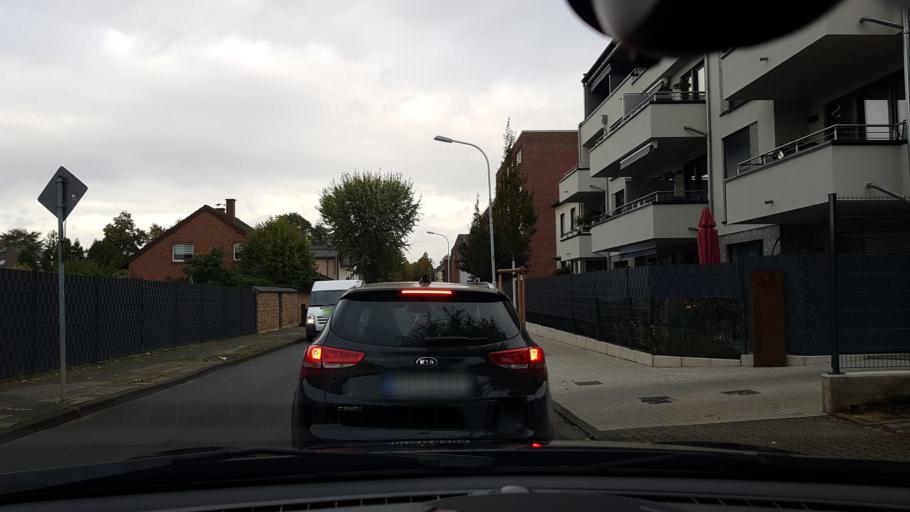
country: DE
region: North Rhine-Westphalia
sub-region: Regierungsbezirk Koln
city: Bergheim
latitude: 50.9550
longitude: 6.6486
